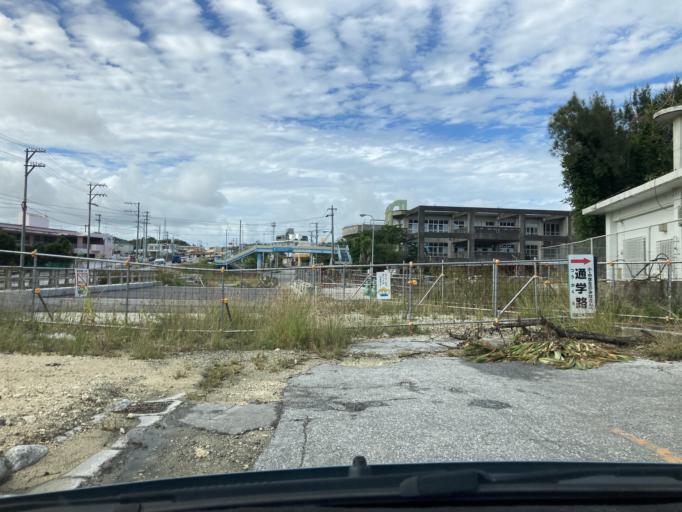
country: JP
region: Okinawa
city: Tomigusuku
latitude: 26.1507
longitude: 127.7235
